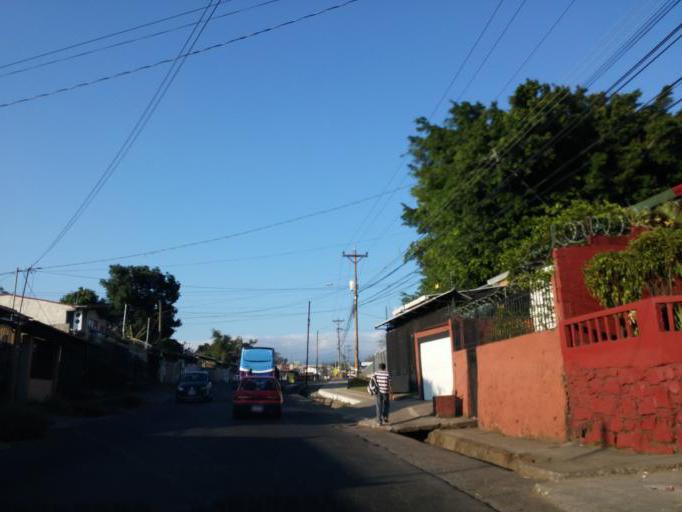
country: CR
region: Alajuela
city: Alajuela
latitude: 10.0052
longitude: -84.2182
